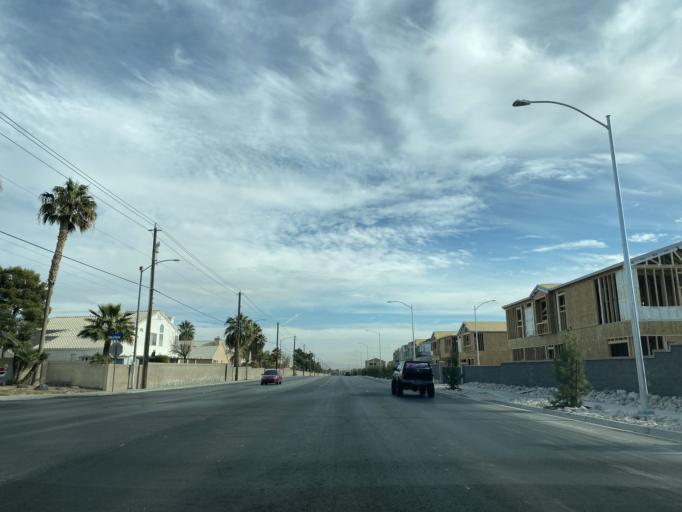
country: US
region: Nevada
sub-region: Clark County
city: North Las Vegas
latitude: 36.2467
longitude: -115.1666
